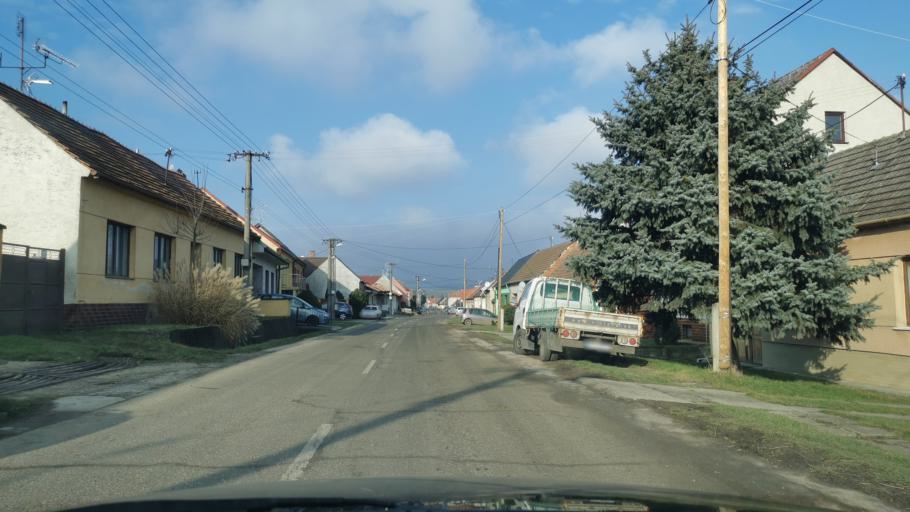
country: SK
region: Trnavsky
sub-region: Okres Skalica
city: Skalica
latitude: 48.7619
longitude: 17.2825
